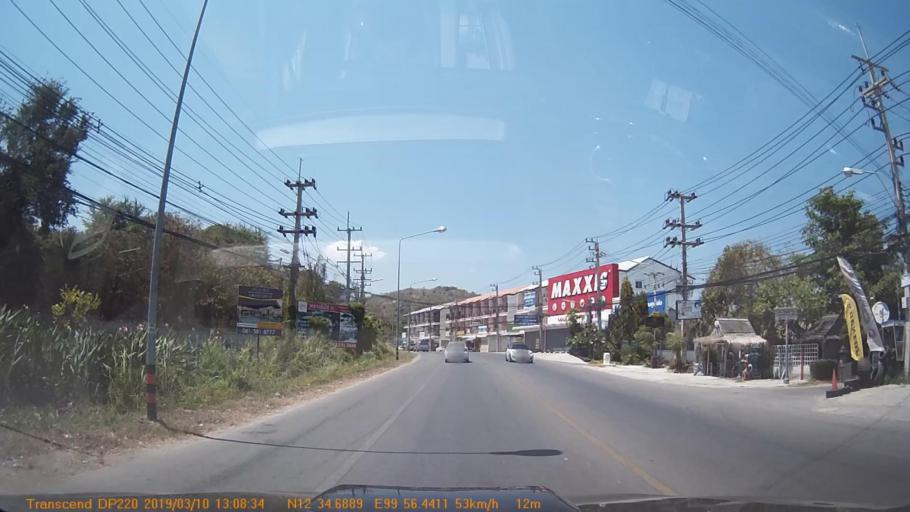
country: TH
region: Prachuap Khiri Khan
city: Hua Hin
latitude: 12.5782
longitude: 99.9406
